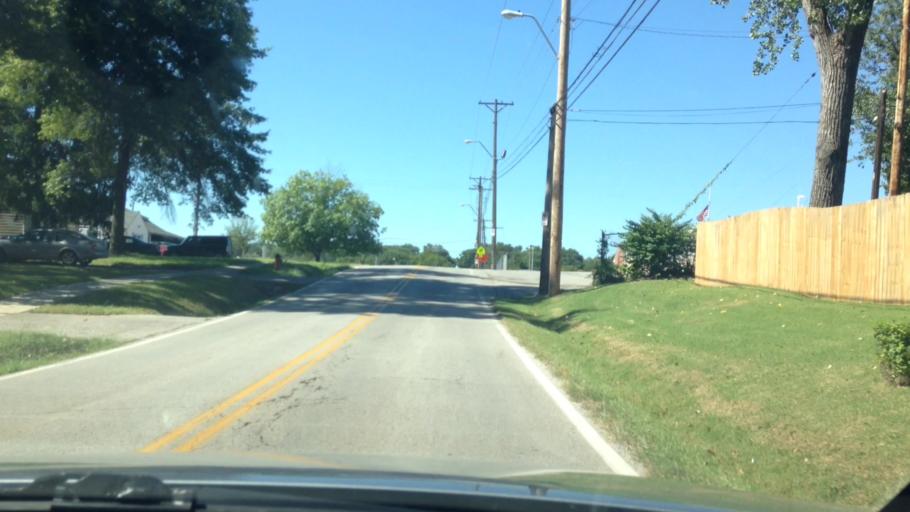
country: US
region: Kansas
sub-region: Johnson County
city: Leawood
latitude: 38.9668
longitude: -94.5926
